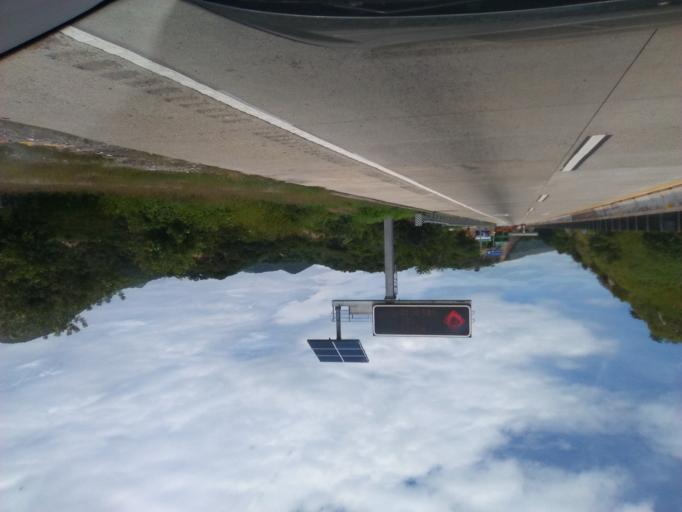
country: MX
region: Guerrero
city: Tierra Colorada
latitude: 17.1723
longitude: -99.5540
